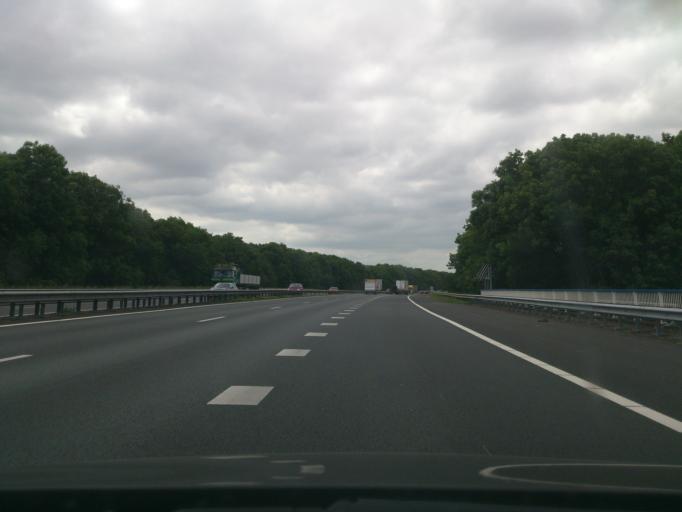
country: NL
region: Gelderland
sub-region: Gemeente Wijchen
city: Bergharen
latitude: 51.8062
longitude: 5.6765
